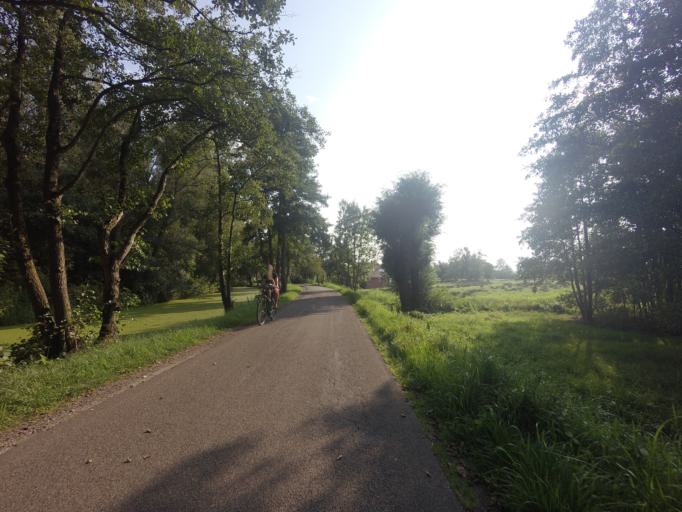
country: NL
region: Groningen
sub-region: Gemeente Haren
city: Haren
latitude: 53.1741
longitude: 6.5810
